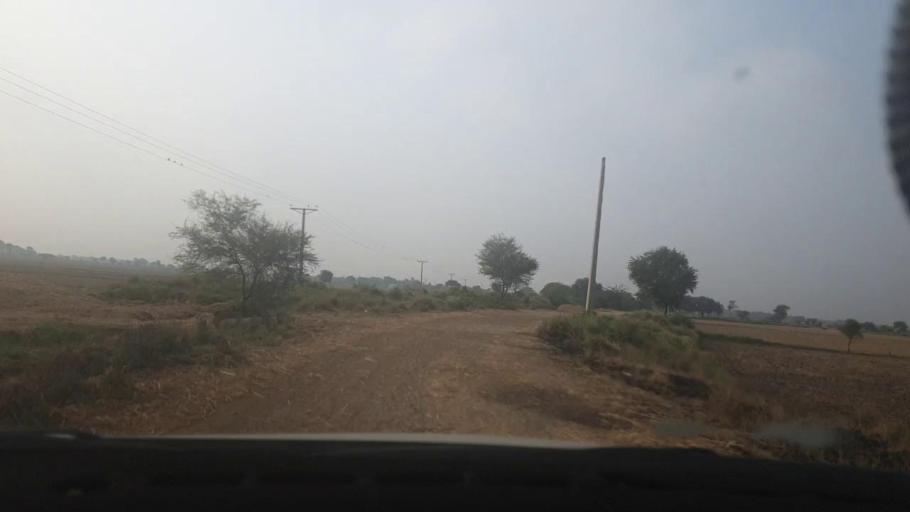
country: PK
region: Sindh
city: Tando Muhammad Khan
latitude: 25.0836
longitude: 68.5143
